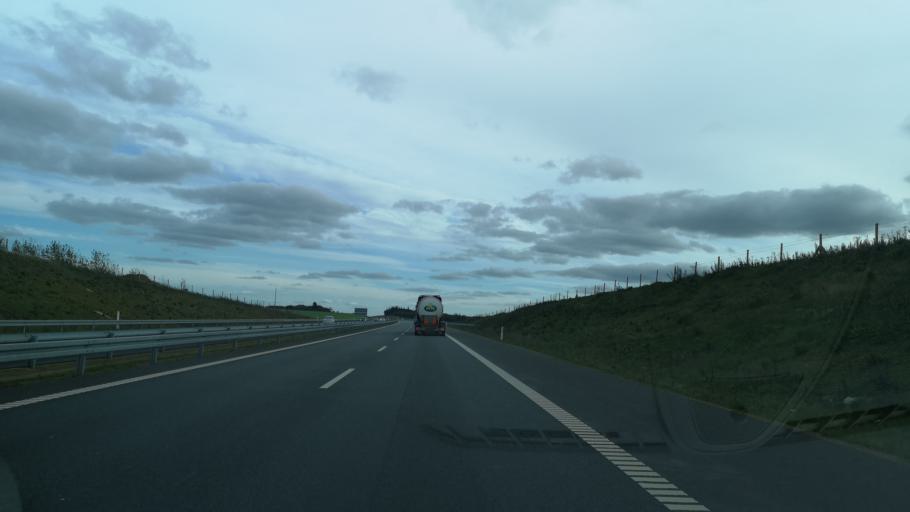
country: DK
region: Central Jutland
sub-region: Herning Kommune
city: Avlum
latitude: 56.2782
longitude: 8.7413
